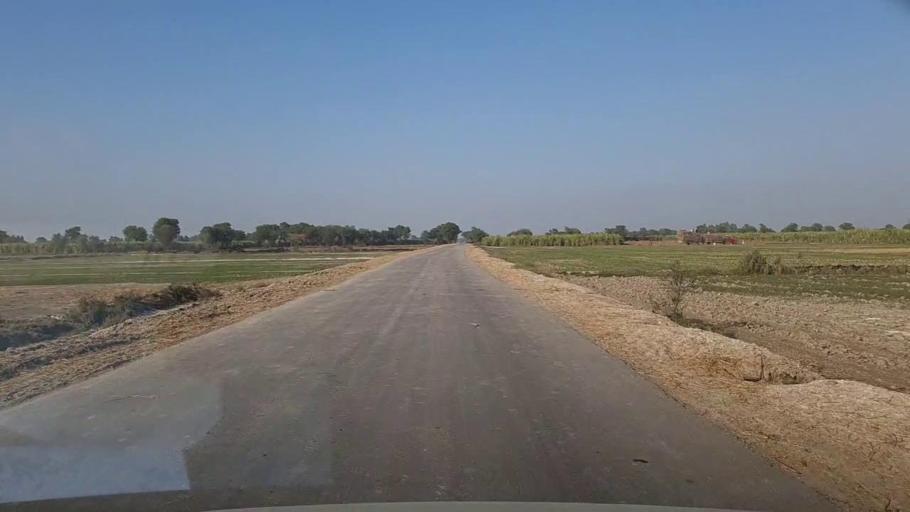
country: PK
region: Sindh
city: Dadu
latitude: 26.8466
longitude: 67.7938
